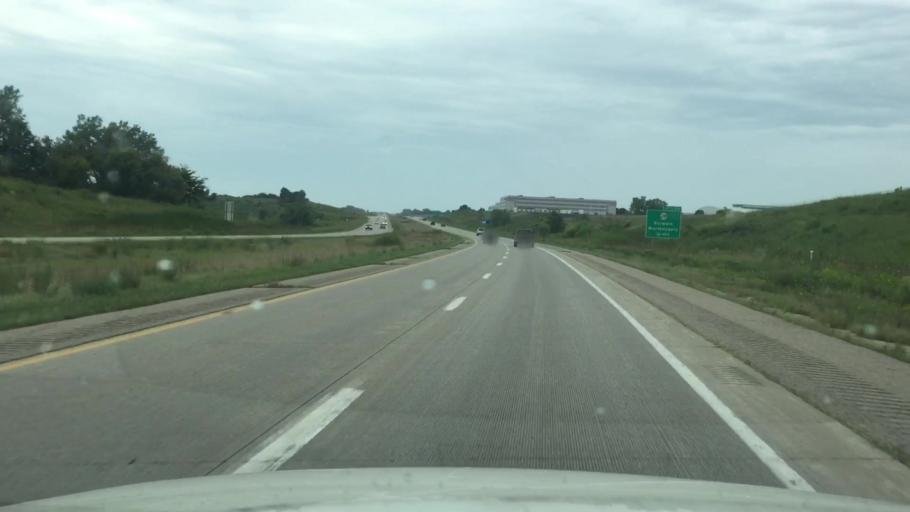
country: US
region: Iowa
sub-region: Warren County
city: Norwalk
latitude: 41.5143
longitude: -93.6623
